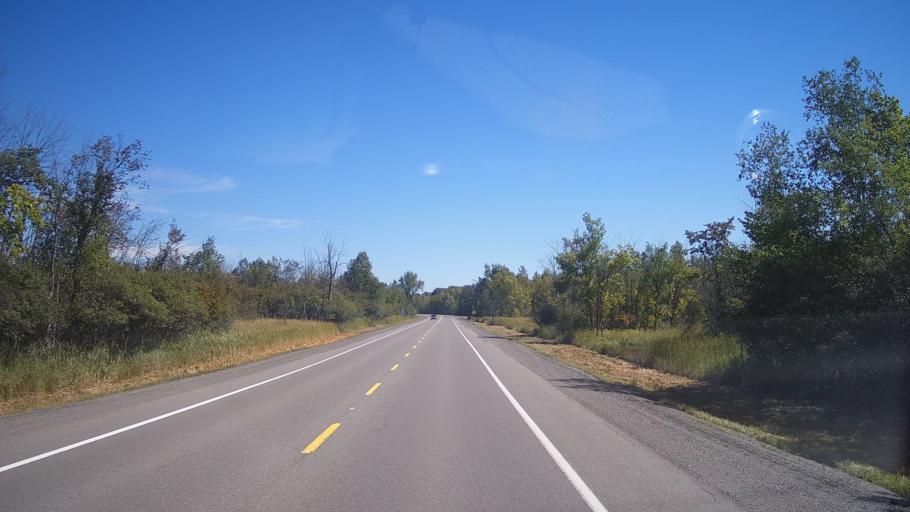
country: CA
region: Ontario
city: Bells Corners
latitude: 45.0684
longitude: -75.6541
